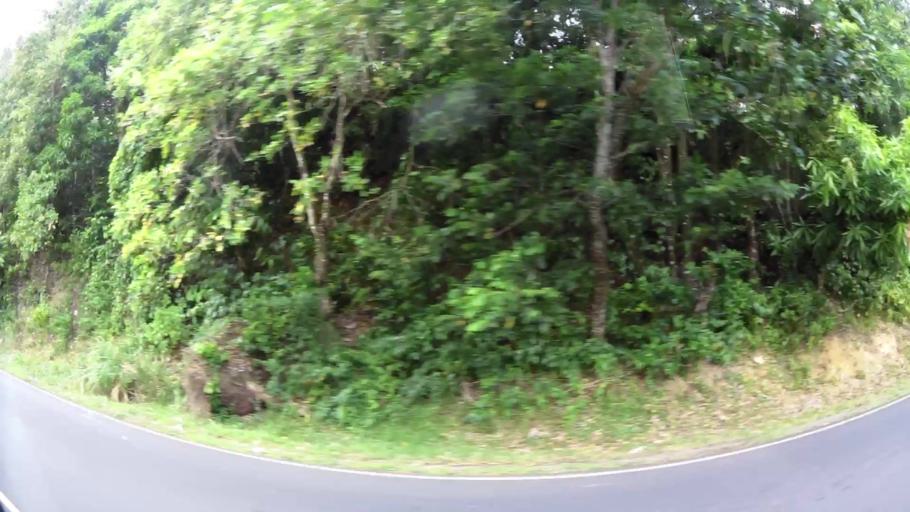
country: LC
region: Dennery Quarter
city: Dennery
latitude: 13.9336
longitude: -60.9377
